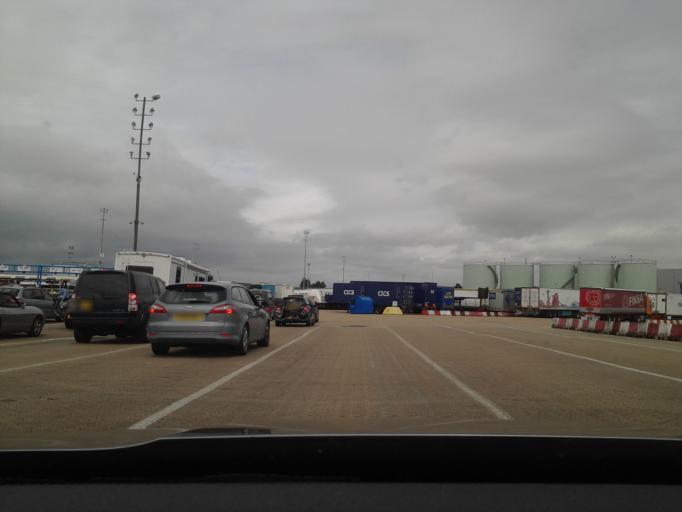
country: GB
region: England
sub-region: Portsmouth
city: Portsmouth
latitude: 50.8128
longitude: -1.0920
